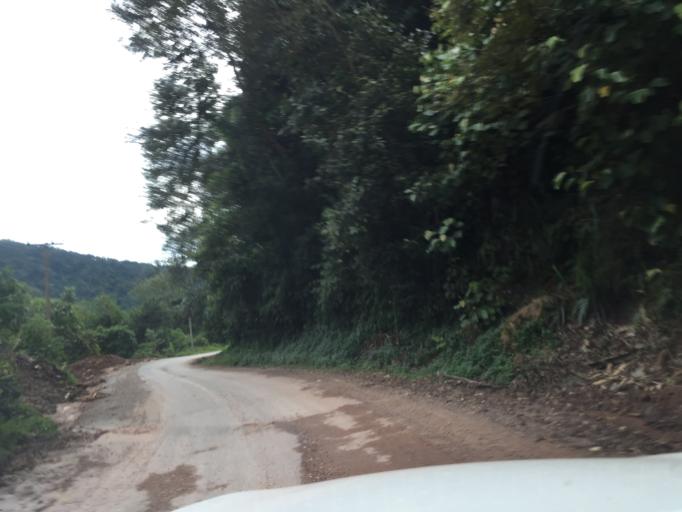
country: LA
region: Phongsali
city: Phongsali
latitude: 21.3320
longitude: 102.0518
